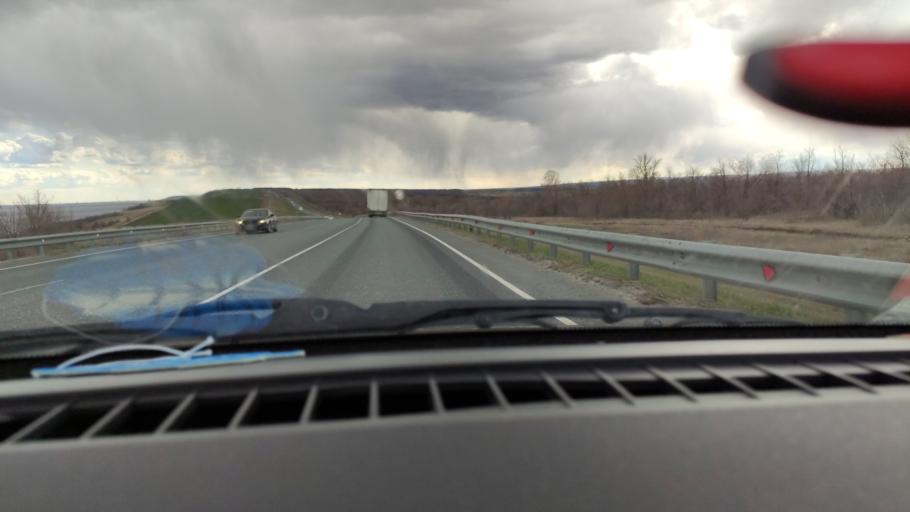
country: RU
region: Saratov
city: Balakovo
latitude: 52.1984
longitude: 47.8619
